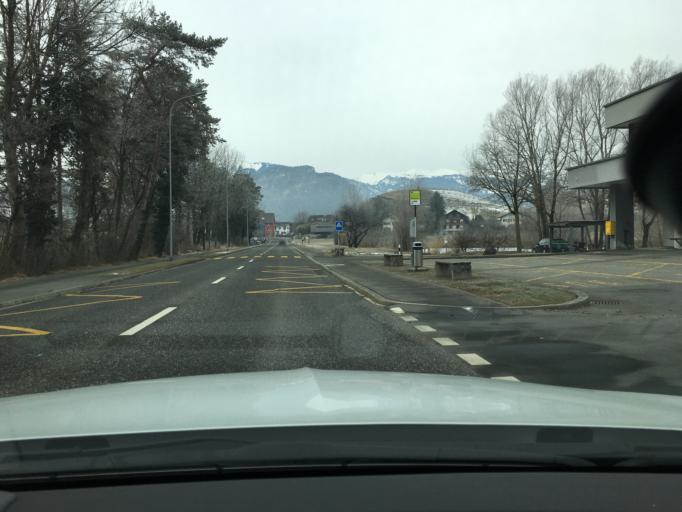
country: LI
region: Balzers
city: Balzers
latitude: 47.0639
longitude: 9.5036
